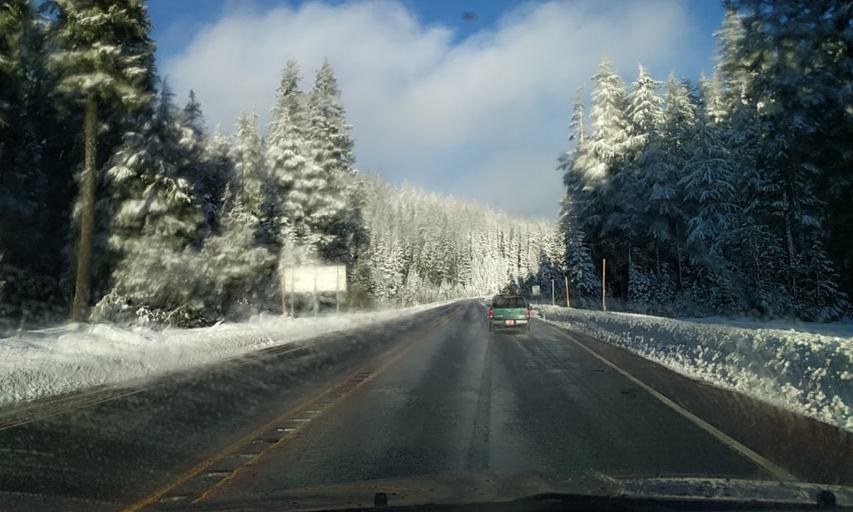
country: US
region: Oregon
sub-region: Clackamas County
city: Mount Hood Village
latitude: 45.2861
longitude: -121.7024
